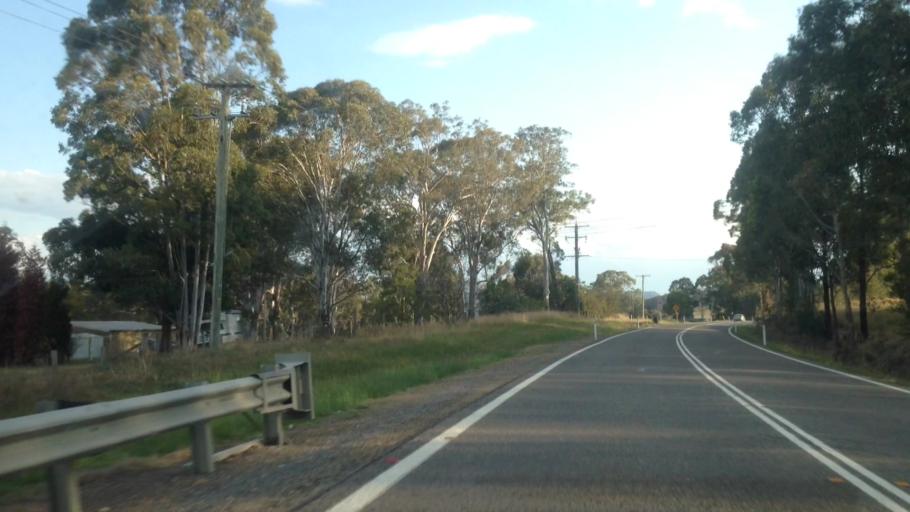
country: AU
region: New South Wales
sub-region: Cessnock
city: Kurri Kurri
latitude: -32.8698
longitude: 151.4793
